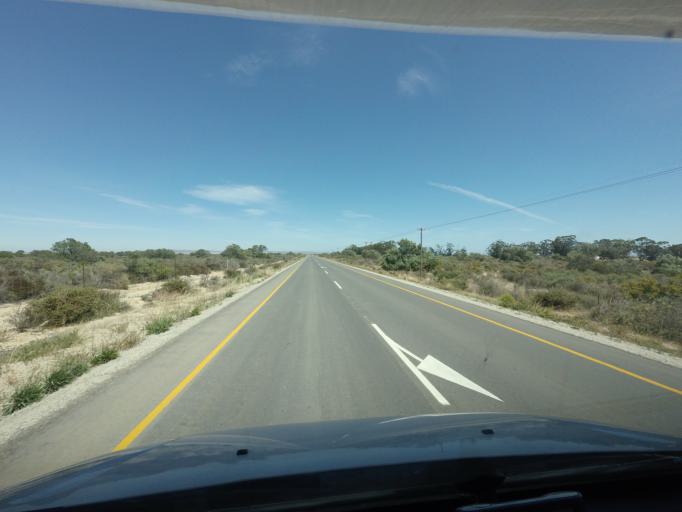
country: ZA
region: Western Cape
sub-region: West Coast District Municipality
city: Vredenburg
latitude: -32.7949
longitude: 18.2452
